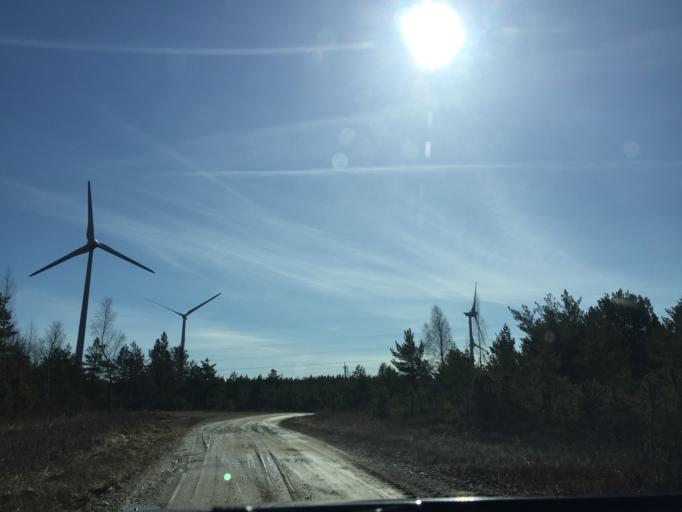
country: EE
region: Laeaene
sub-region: Haapsalu linn
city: Haapsalu
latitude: 58.6353
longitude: 23.5232
